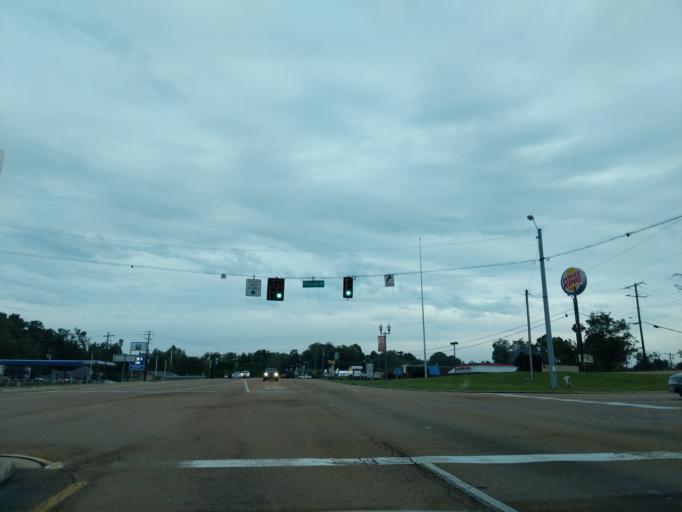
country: US
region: Mississippi
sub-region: Warren County
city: Vicksburg
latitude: 32.3217
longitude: -90.8769
